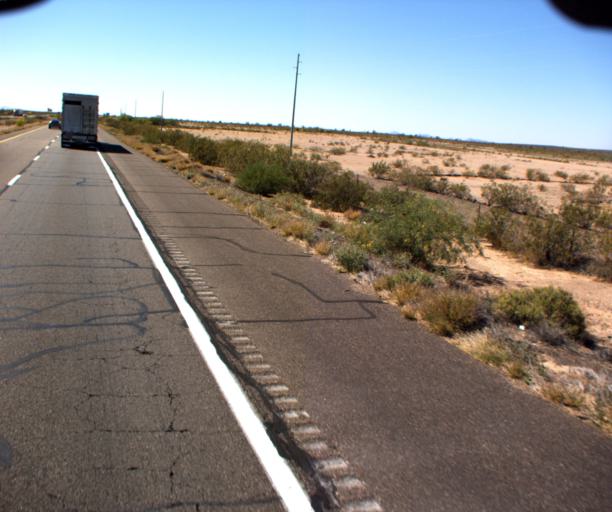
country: US
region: Arizona
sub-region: Maricopa County
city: Gila Bend
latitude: 32.8573
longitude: -113.2264
